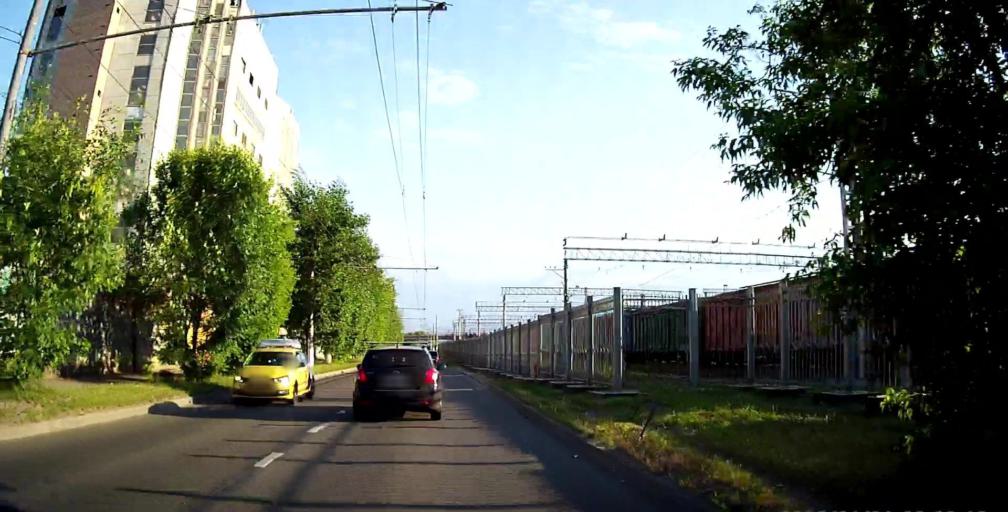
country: RU
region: Moskovskaya
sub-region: Podol'skiy Rayon
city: Podol'sk
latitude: 55.4287
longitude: 37.5647
